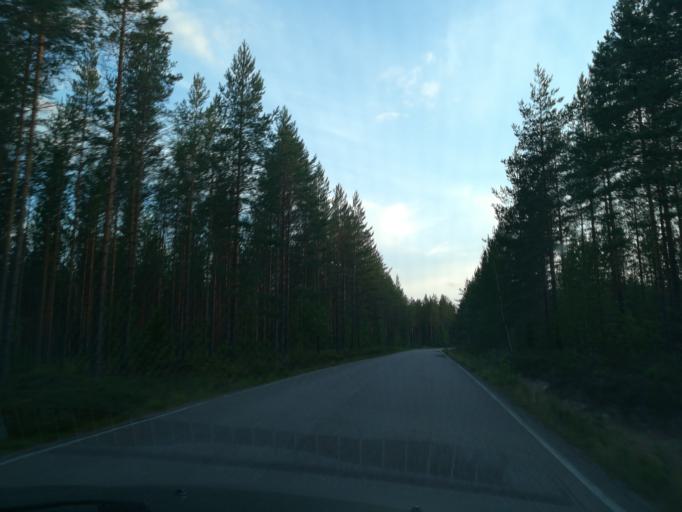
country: FI
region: South Karelia
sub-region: Lappeenranta
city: Joutseno
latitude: 61.3445
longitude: 28.4105
